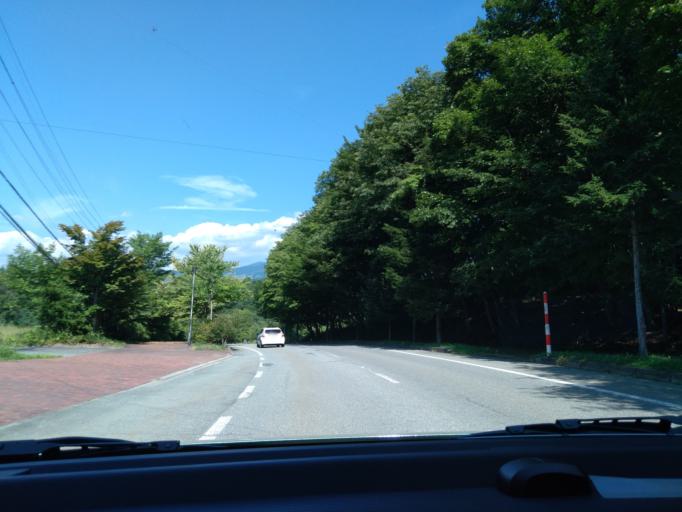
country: JP
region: Akita
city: Kakunodatemachi
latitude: 39.7346
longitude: 140.7010
